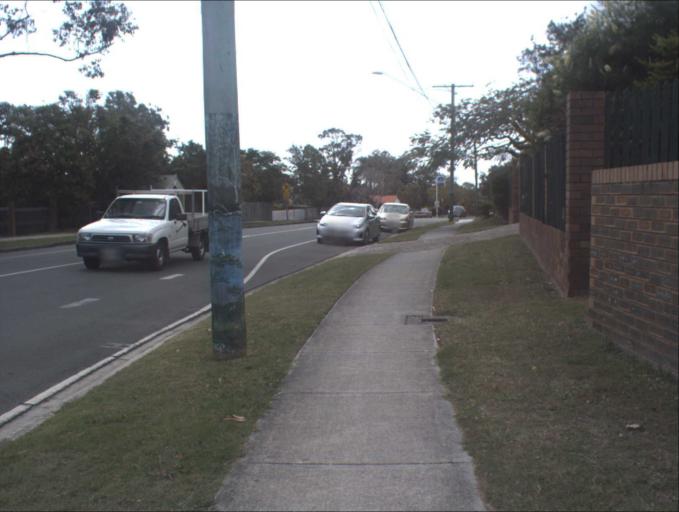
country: AU
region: Queensland
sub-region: Logan
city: Park Ridge South
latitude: -27.6694
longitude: 153.0377
